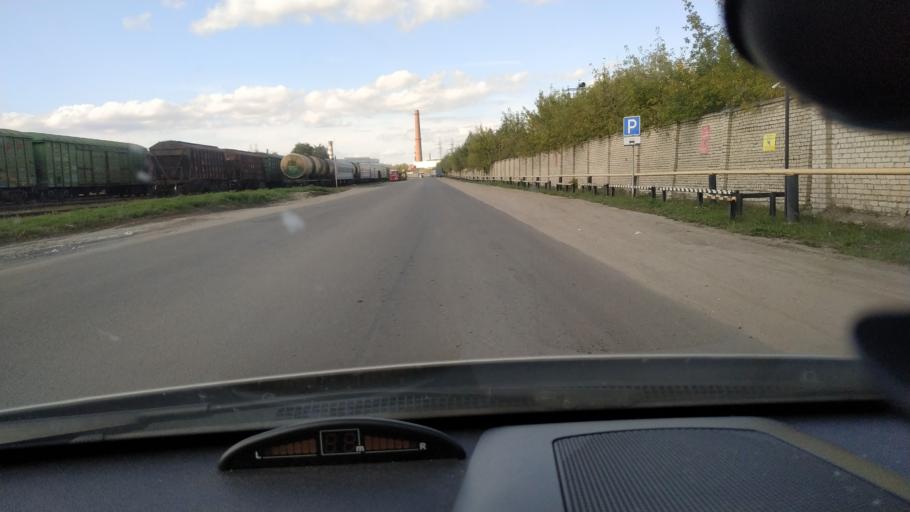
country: RU
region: Rjazan
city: Ryazan'
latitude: 54.6647
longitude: 39.6261
